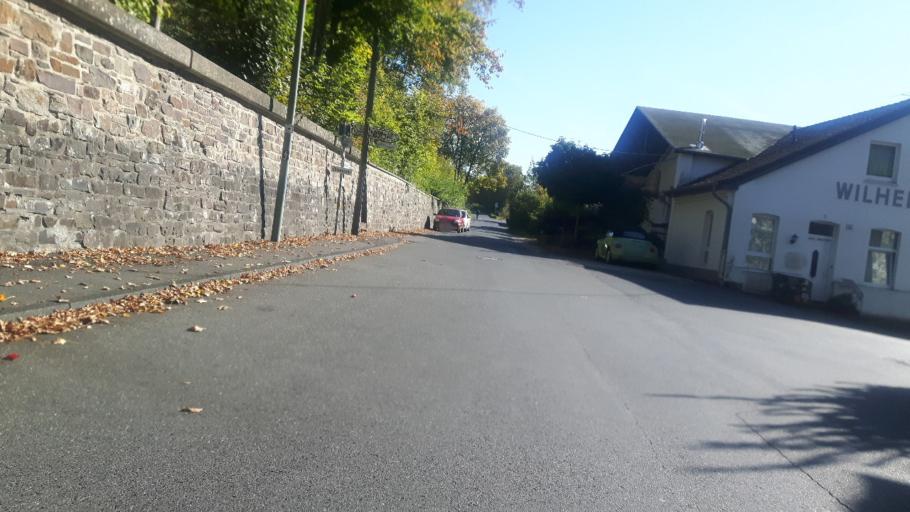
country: DE
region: Rheinland-Pfalz
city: Niederirsen
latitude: 50.8069
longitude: 7.5906
